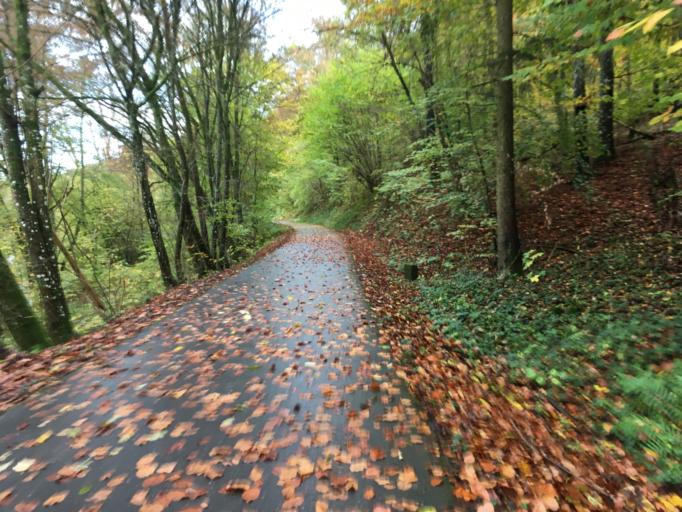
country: DE
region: Baden-Wuerttemberg
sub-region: Regierungsbezirk Stuttgart
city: Mockmuhl
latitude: 49.3102
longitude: 9.3884
